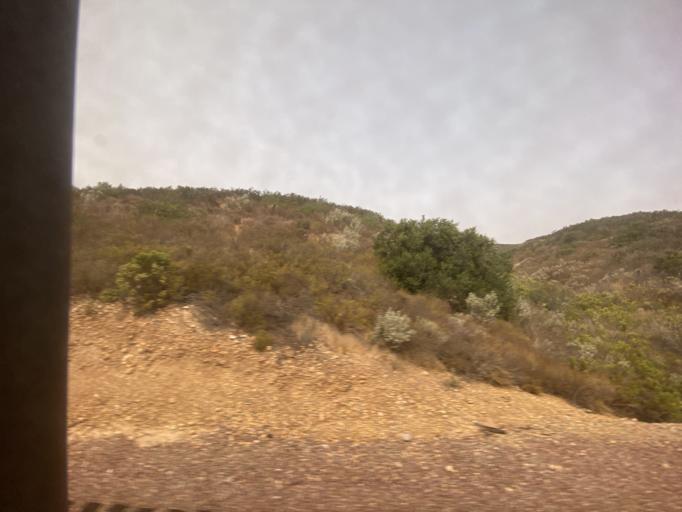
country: US
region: California
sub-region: San Diego County
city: La Jolla
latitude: 32.8690
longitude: -117.1827
